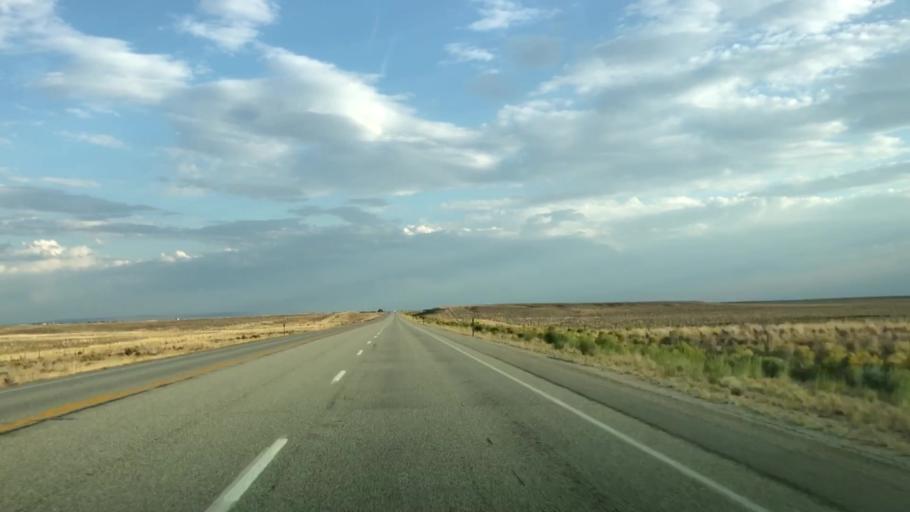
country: US
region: Wyoming
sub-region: Sweetwater County
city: North Rock Springs
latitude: 42.1841
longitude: -109.4784
